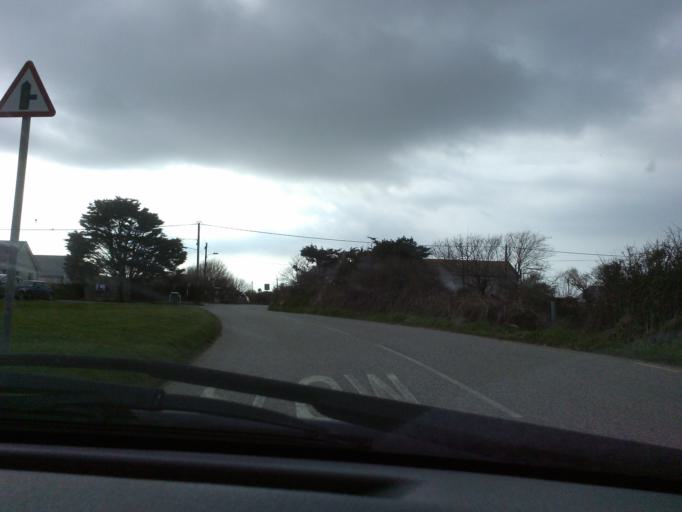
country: GB
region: England
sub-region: Cornwall
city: St. Buryan
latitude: 50.0563
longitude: -5.6606
